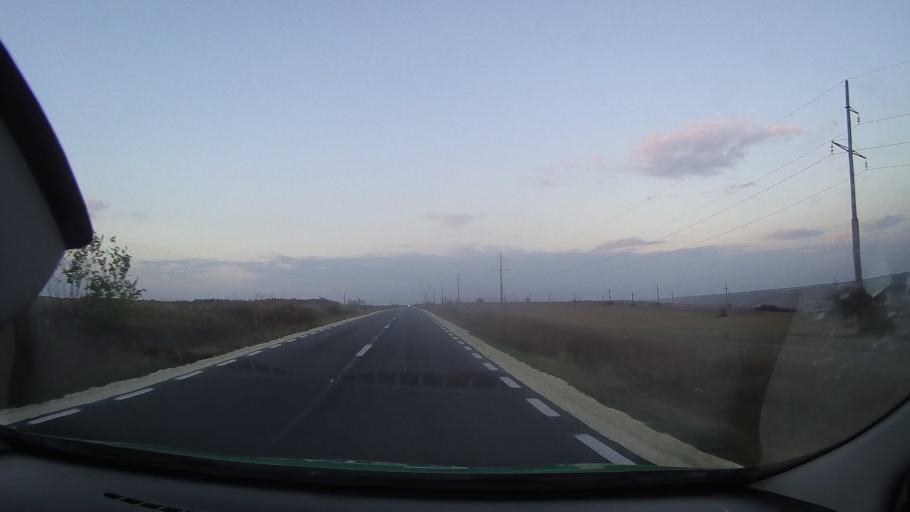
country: RO
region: Constanta
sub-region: Comuna Baneasa
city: Baneasa
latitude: 44.0848
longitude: 27.6883
